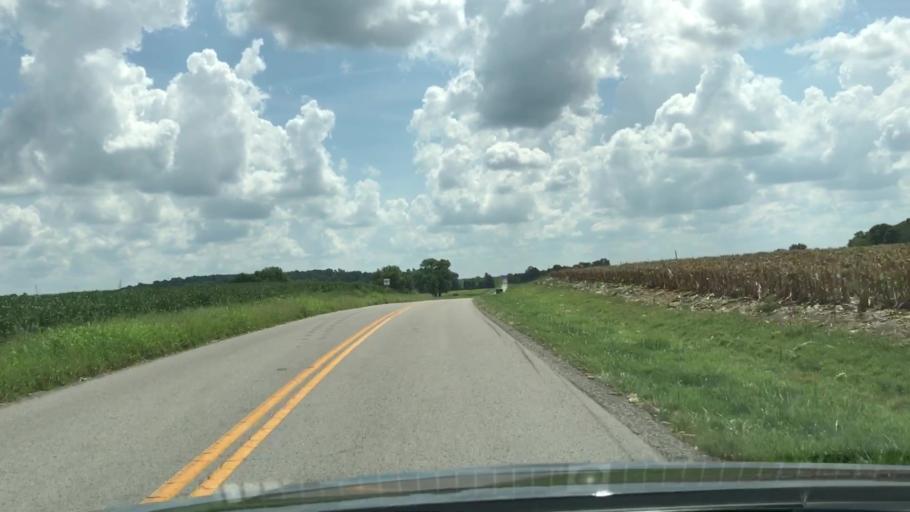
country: US
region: Kentucky
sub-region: Todd County
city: Guthrie
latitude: 36.7078
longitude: -87.0476
